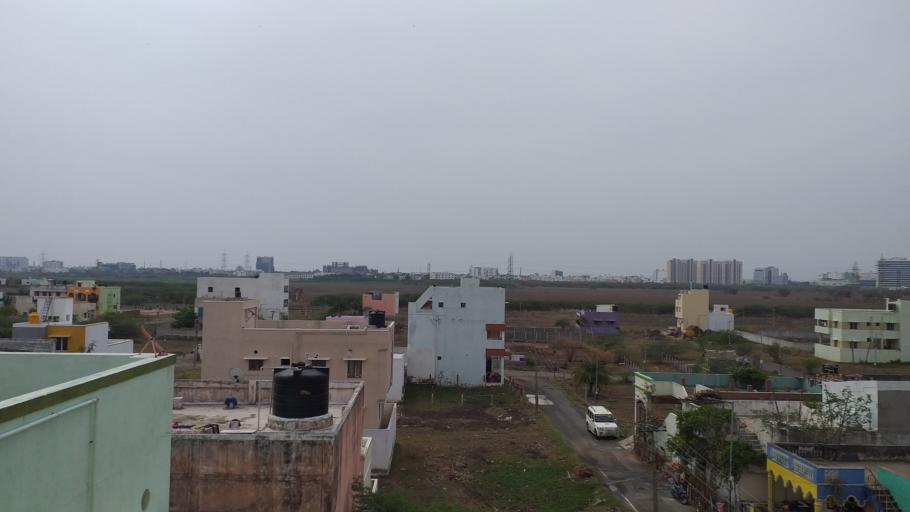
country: IN
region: Tamil Nadu
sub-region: Kancheepuram
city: Injambakkam
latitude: 12.9231
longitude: 80.2104
